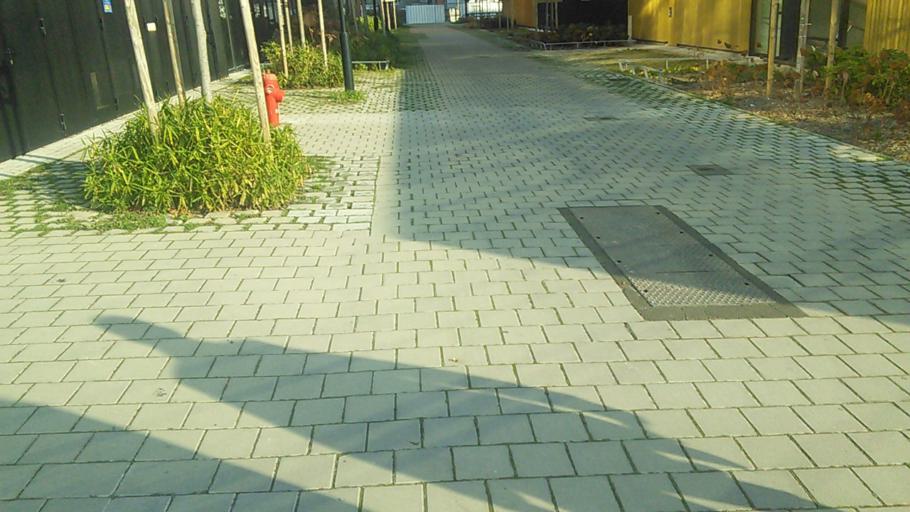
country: FR
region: Pays de la Loire
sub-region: Departement de la Loire-Atlantique
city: Nantes
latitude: 47.2167
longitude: -1.5357
